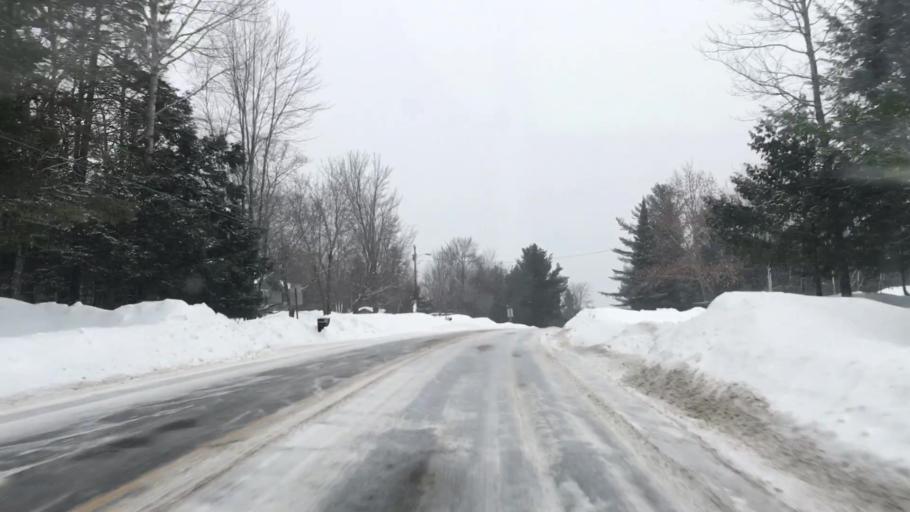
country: US
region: Maine
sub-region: Penobscot County
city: Medway
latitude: 45.5231
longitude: -68.3552
